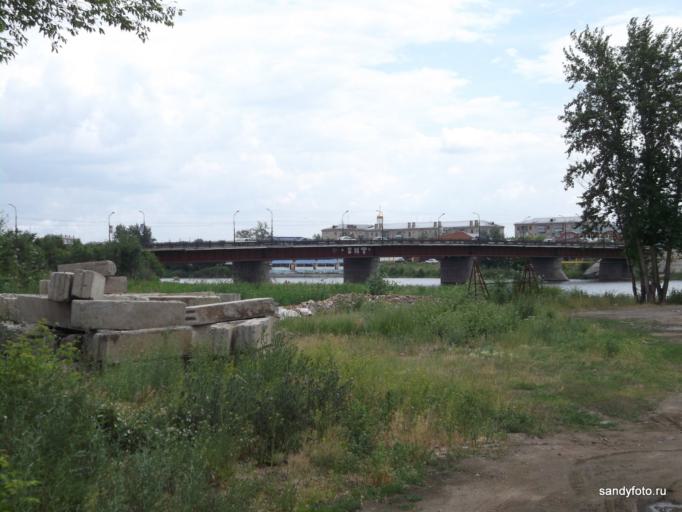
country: RU
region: Chelyabinsk
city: Troitsk
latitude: 54.0940
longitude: 61.5662
